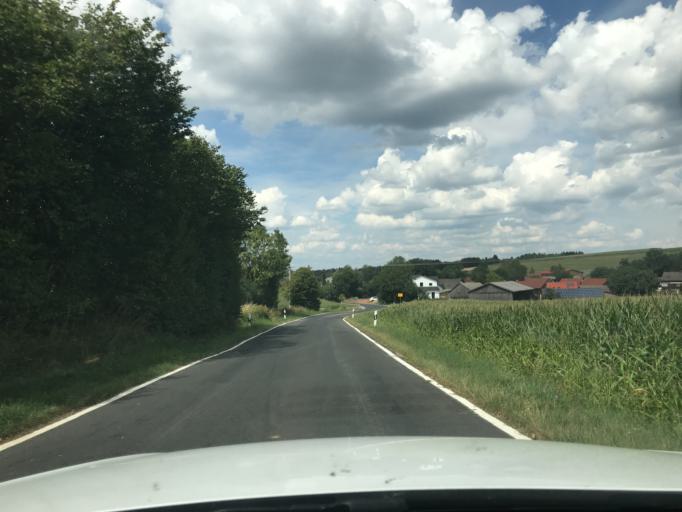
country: DE
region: Bavaria
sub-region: Upper Palatinate
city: Auerbach
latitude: 49.7391
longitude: 11.6378
